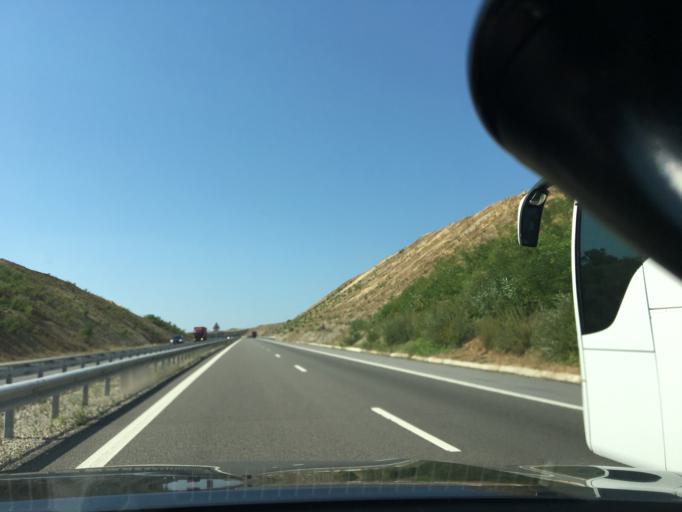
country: BG
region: Kyustendil
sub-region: Obshtina Dupnitsa
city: Dupnitsa
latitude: 42.2973
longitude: 23.0921
